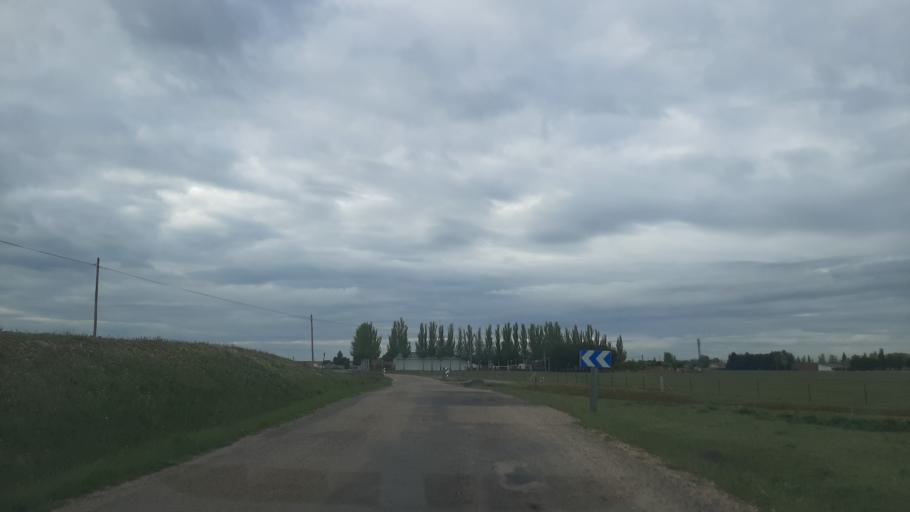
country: ES
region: Castille and Leon
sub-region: Provincia de Salamanca
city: Palaciosrubios
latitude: 41.0589
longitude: -5.1986
